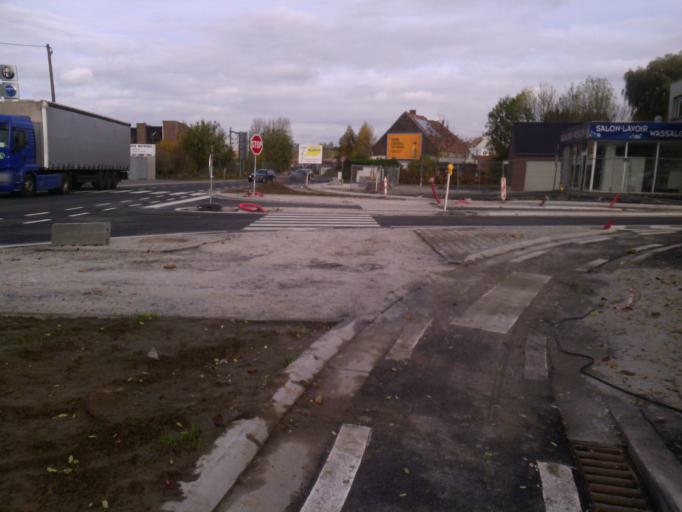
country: BE
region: Wallonia
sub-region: Province du Hainaut
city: Mouscron
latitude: 50.7654
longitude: 3.2191
